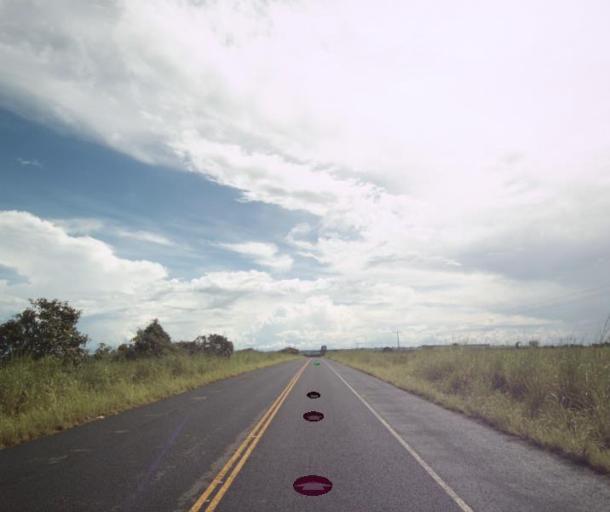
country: BR
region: Goias
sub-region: Sao Miguel Do Araguaia
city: Sao Miguel do Araguaia
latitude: -13.3011
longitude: -50.2618
